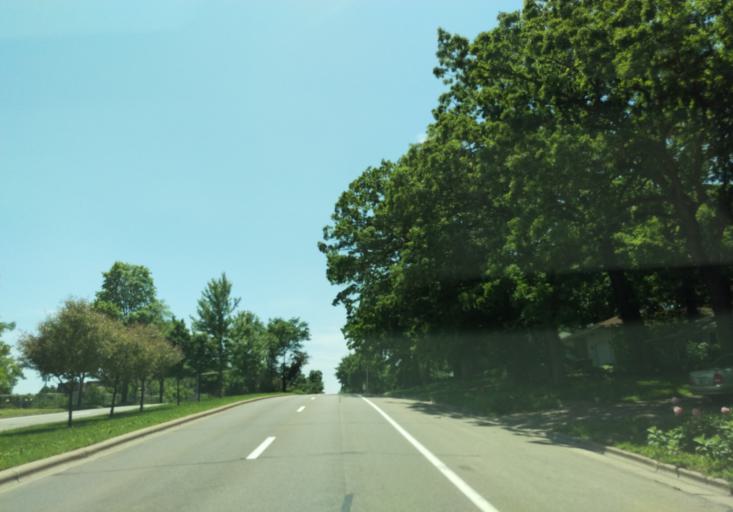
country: US
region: Wisconsin
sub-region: Dane County
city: Shorewood Hills
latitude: 43.0572
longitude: -89.4512
